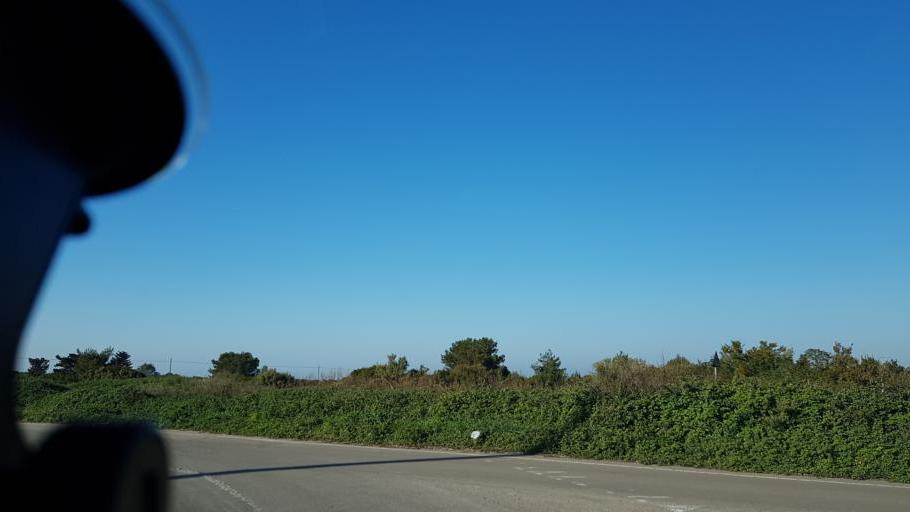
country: IT
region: Apulia
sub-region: Provincia di Lecce
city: Merine
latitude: 40.4091
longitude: 18.2585
